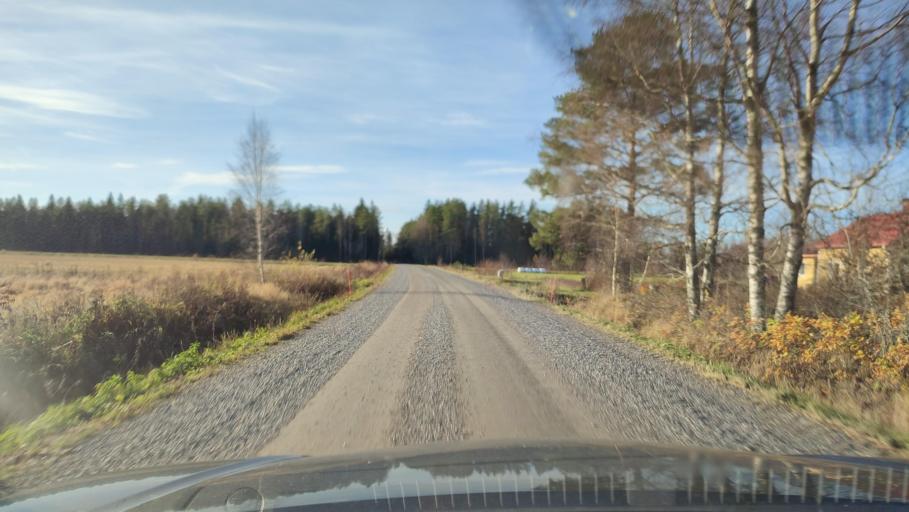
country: FI
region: Southern Ostrobothnia
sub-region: Suupohja
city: Teuva
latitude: 62.4554
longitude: 21.6219
